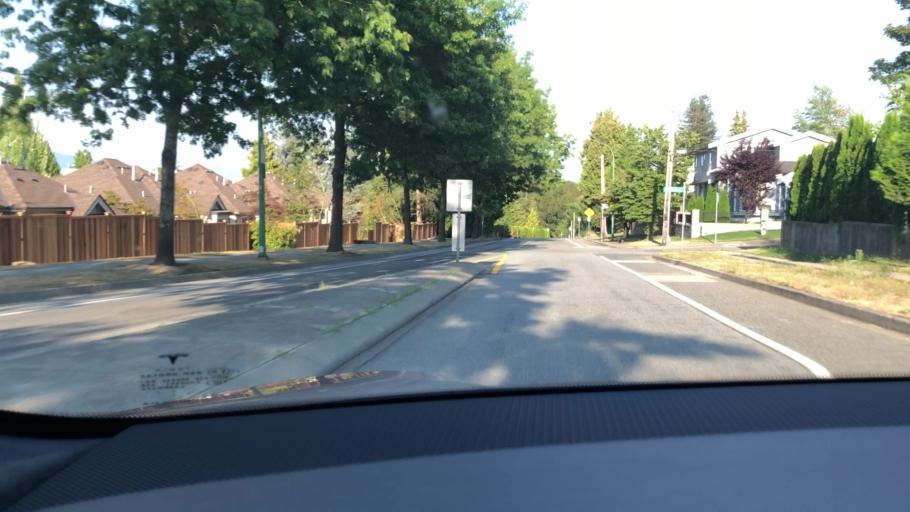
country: CA
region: British Columbia
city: Burnaby
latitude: 49.2296
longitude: -122.9846
